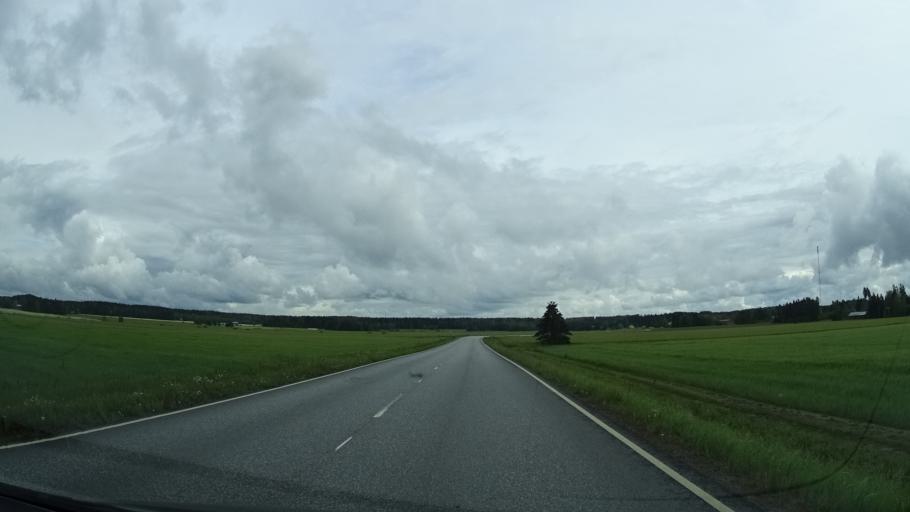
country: FI
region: Haeme
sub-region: Forssa
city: Humppila
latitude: 61.0993
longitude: 23.3001
